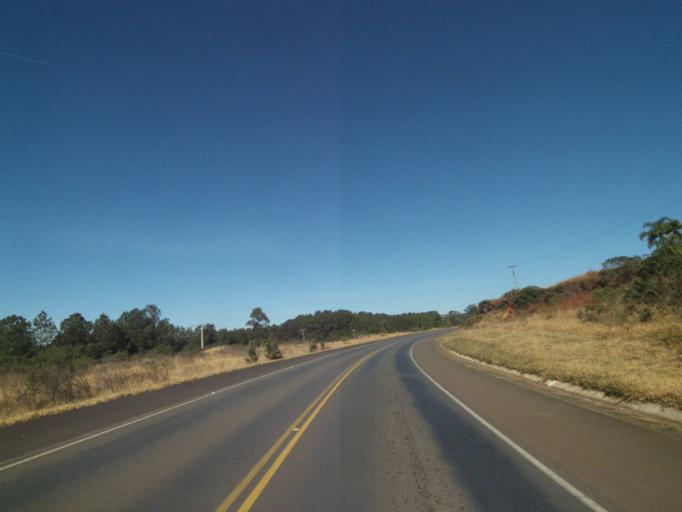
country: BR
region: Parana
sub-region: Tibagi
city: Tibagi
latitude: -24.4890
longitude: -50.4384
